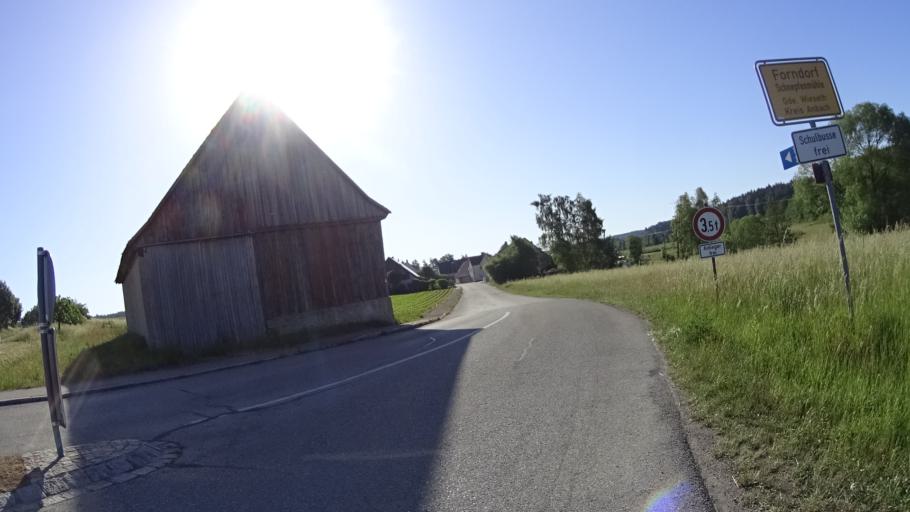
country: DE
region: Bavaria
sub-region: Regierungsbezirk Mittelfranken
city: Wieseth
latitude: 49.1605
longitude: 10.4986
